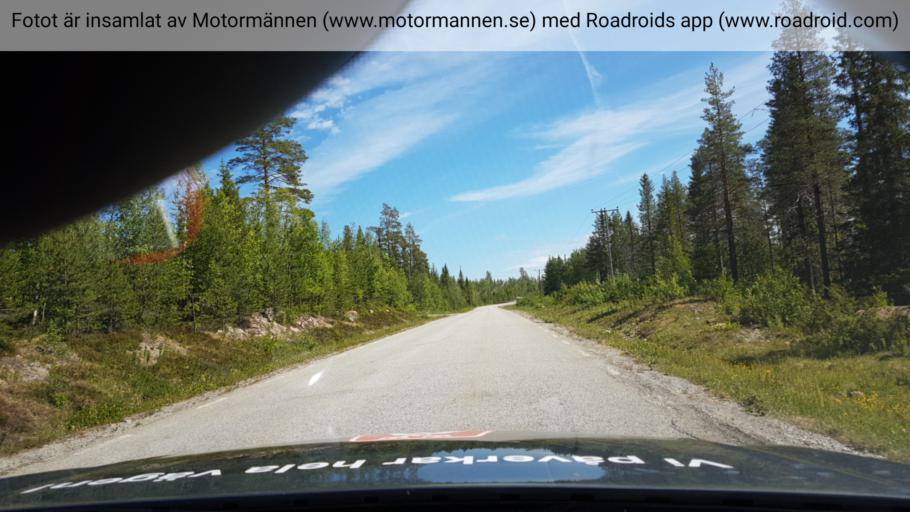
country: SE
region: Jaemtland
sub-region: Bergs Kommun
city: Hoverberg
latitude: 62.6769
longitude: 14.6737
